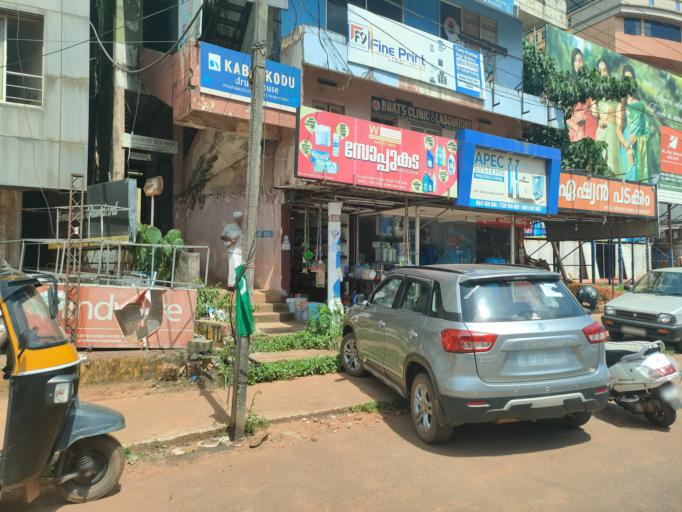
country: IN
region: Kerala
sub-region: Kasaragod District
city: Kasaragod
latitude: 12.5083
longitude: 74.9955
